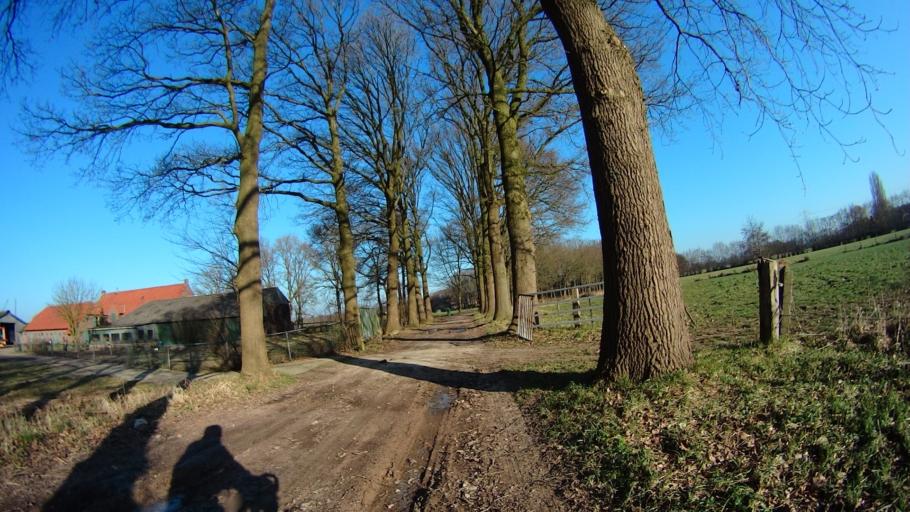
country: NL
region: Utrecht
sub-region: Gemeente Amersfoort
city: Hoogland
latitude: 52.1791
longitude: 5.3456
